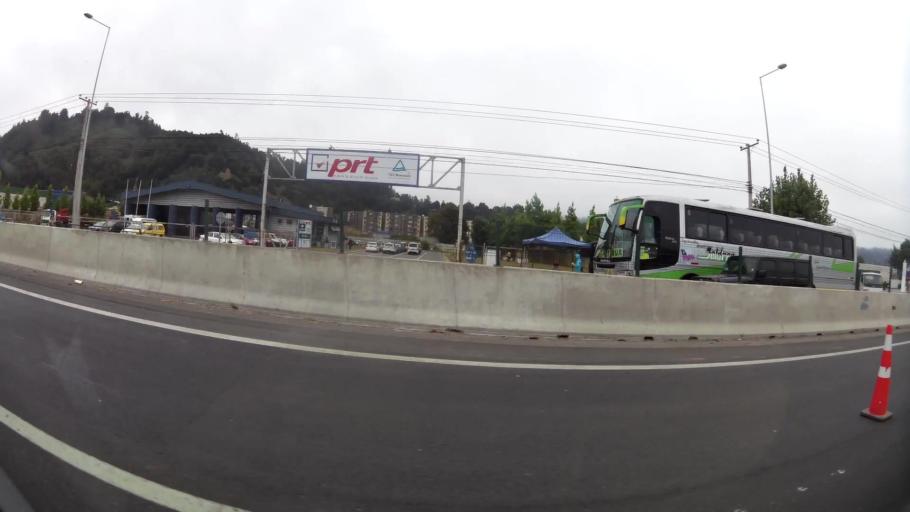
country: CL
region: Biobio
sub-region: Provincia de Concepcion
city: Concepcion
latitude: -36.8200
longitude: -73.0030
